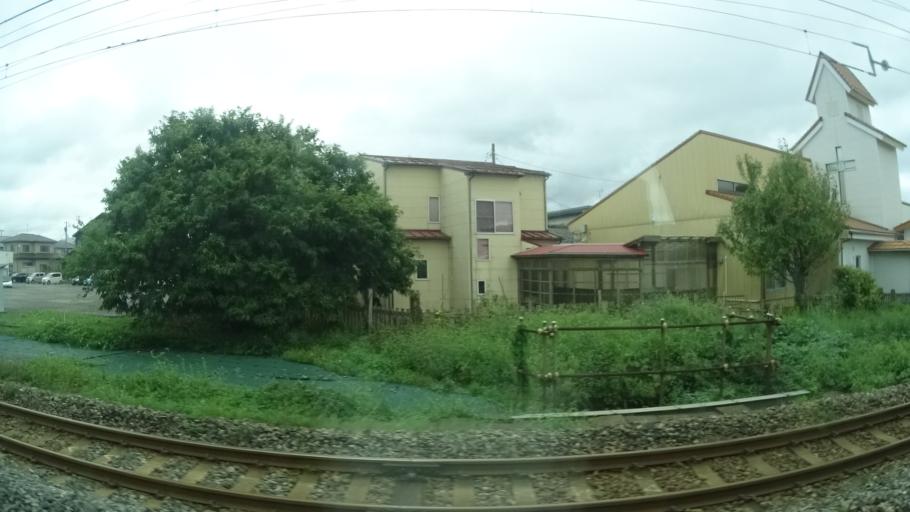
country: JP
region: Niigata
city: Murakami
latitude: 38.2160
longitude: 139.4634
